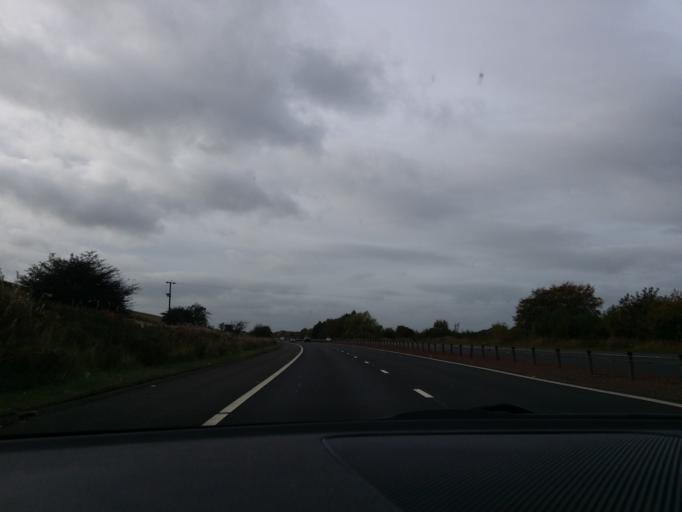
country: GB
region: Scotland
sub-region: West Lothian
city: Linlithgow
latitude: 55.9846
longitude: -3.6352
